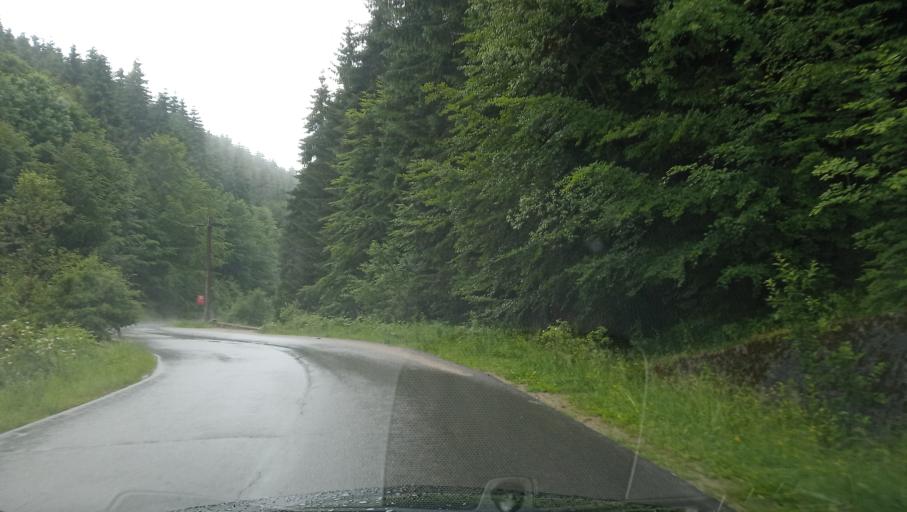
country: RO
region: Hunedoara
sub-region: Oras Petrila
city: Petrila
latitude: 45.3954
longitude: 23.4319
